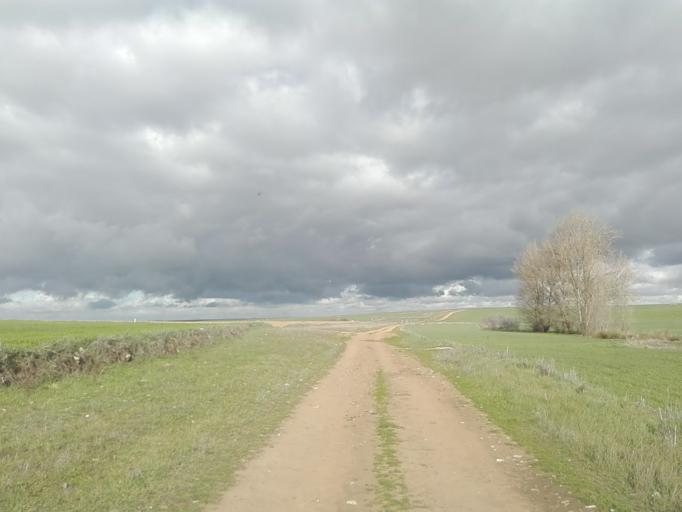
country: ES
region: Extremadura
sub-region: Provincia de Badajoz
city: Llerena
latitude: 38.2774
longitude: -6.0257
